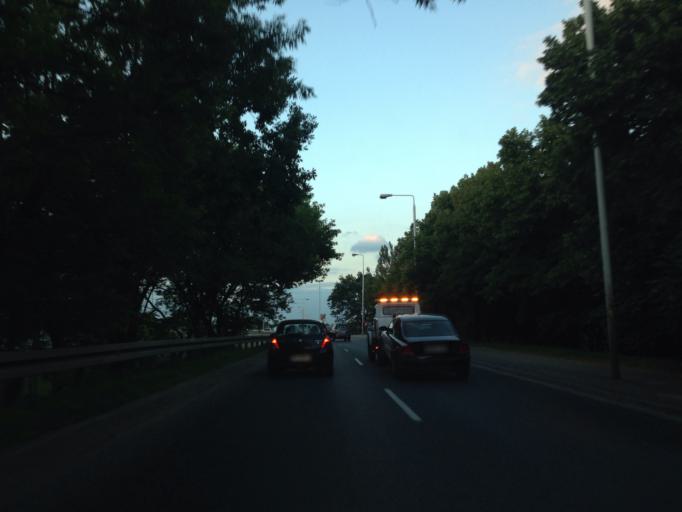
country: PL
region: Masovian Voivodeship
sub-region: Warszawa
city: Zoliborz
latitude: 52.2593
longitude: 21.0052
